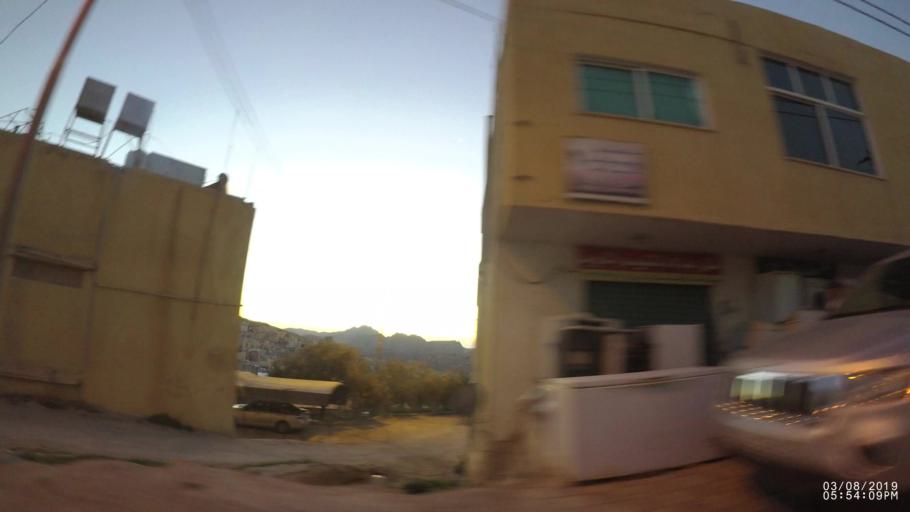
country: JO
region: Ma'an
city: Petra
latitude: 30.3230
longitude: 35.4801
